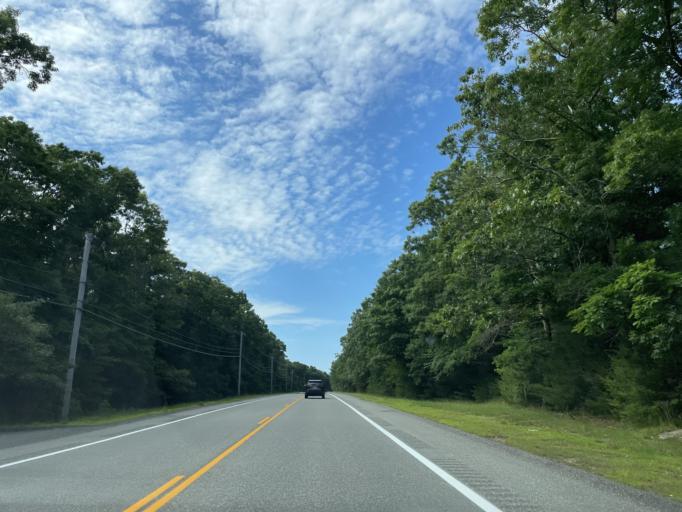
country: US
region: Rhode Island
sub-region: Kent County
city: West Greenwich
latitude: 41.6532
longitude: -71.6940
